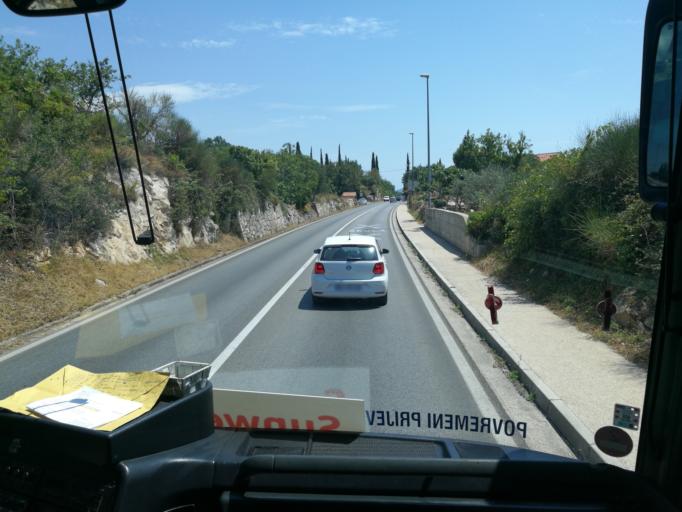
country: HR
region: Dubrovacko-Neretvanska
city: Jasenice
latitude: 42.5633
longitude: 18.2509
